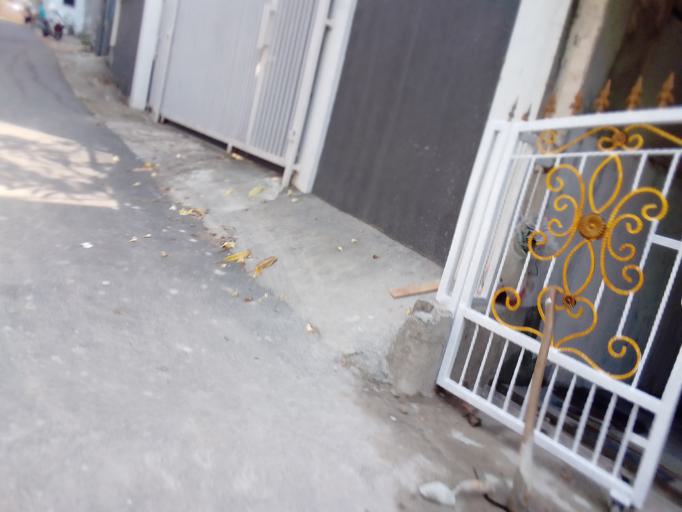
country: ID
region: Jakarta Raya
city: Jakarta
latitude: -6.2174
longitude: 106.7959
